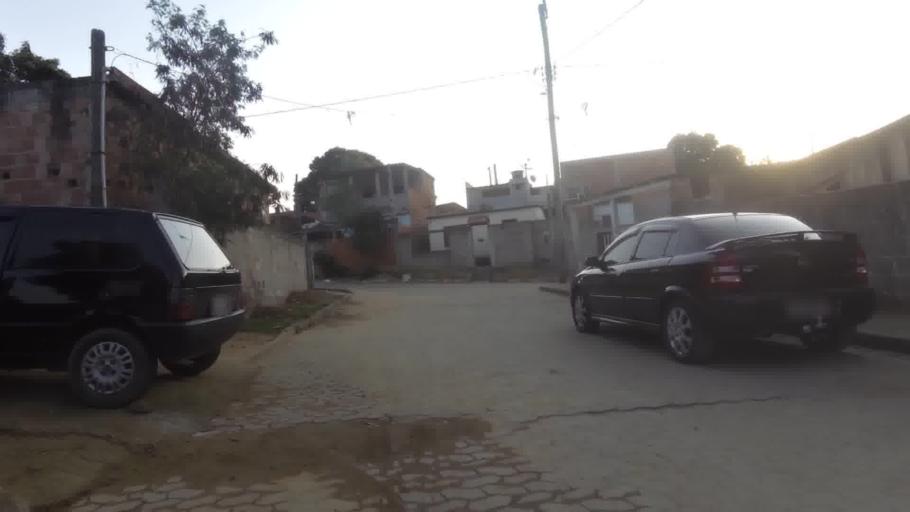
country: BR
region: Espirito Santo
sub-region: Piuma
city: Piuma
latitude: -20.8267
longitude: -40.7198
